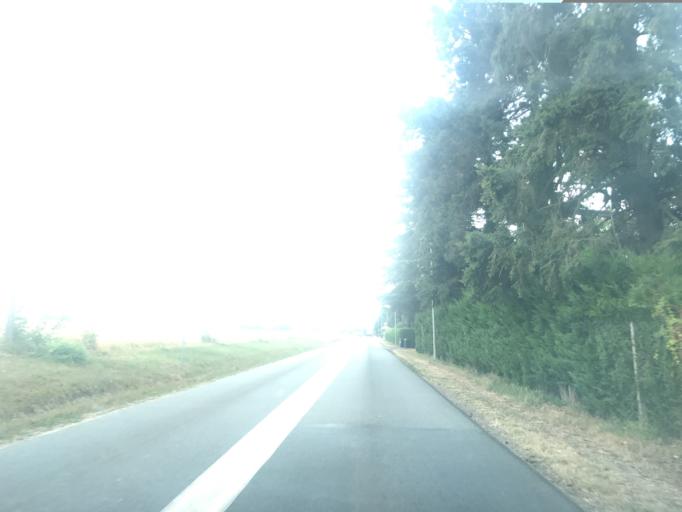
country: FR
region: Haute-Normandie
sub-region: Departement de l'Eure
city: Breuilpont
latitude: 48.9886
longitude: 1.4170
